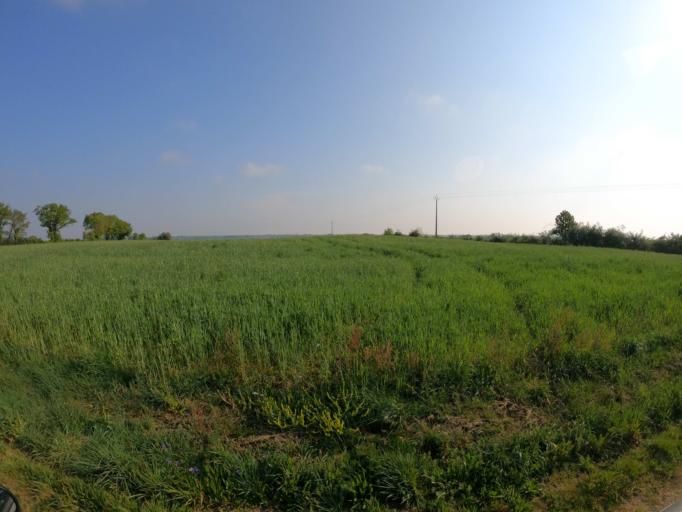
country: FR
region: Pays de la Loire
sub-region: Departement de Maine-et-Loire
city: Saint-Andre-de-la-Marche
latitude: 47.0706
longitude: -0.9831
